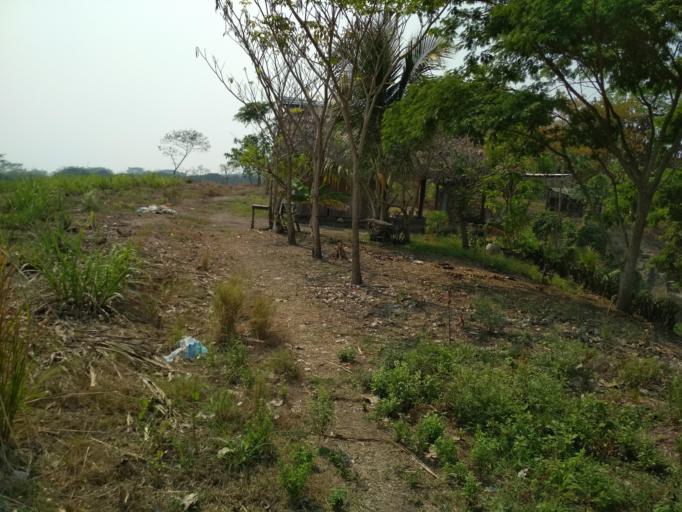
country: MX
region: Oaxaca
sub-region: Acatlan de Perez Figueroa
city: Zona Urbana Ejidal
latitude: 18.5893
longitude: -96.5580
